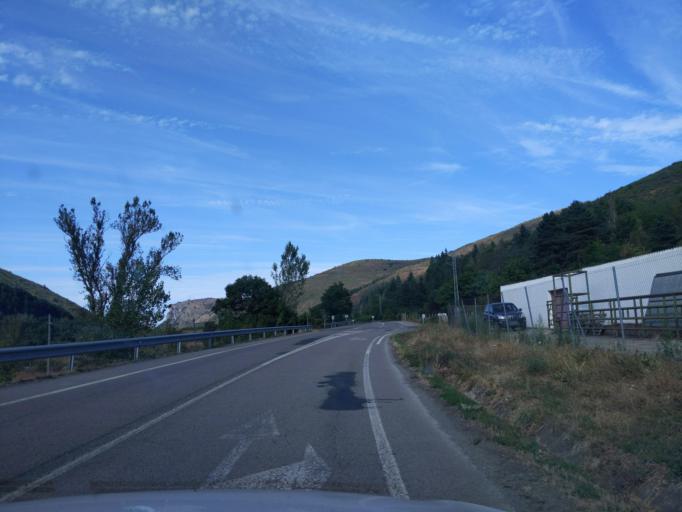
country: ES
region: La Rioja
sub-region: Provincia de La Rioja
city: Ezcaray
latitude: 42.3048
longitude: -3.0221
